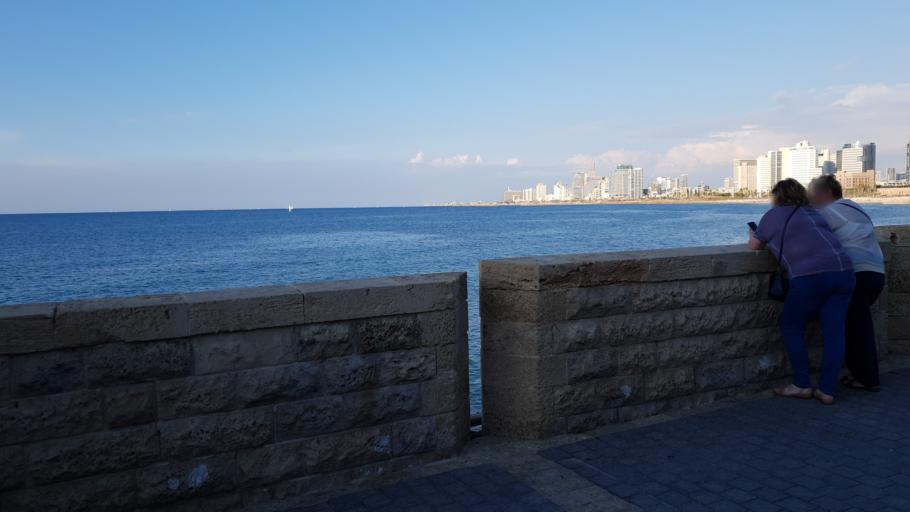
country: IL
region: Tel Aviv
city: Yafo
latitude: 32.0556
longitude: 34.7533
